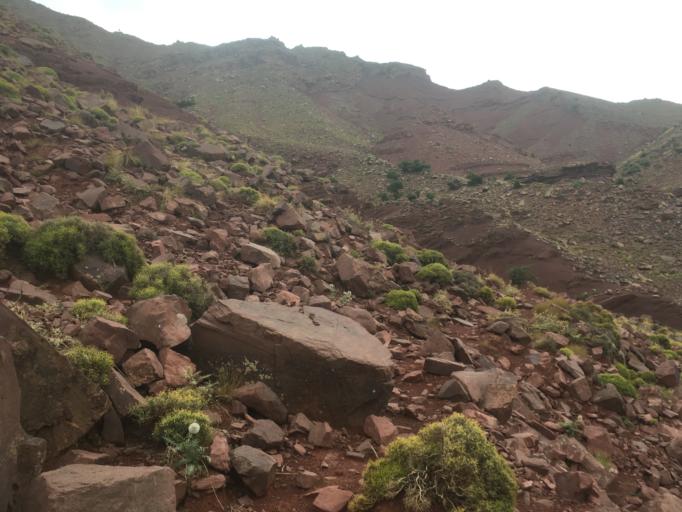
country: MA
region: Marrakech-Tensift-Al Haouz
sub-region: Al-Haouz
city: Tidili Mesfioua
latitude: 31.3277
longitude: -7.6589
